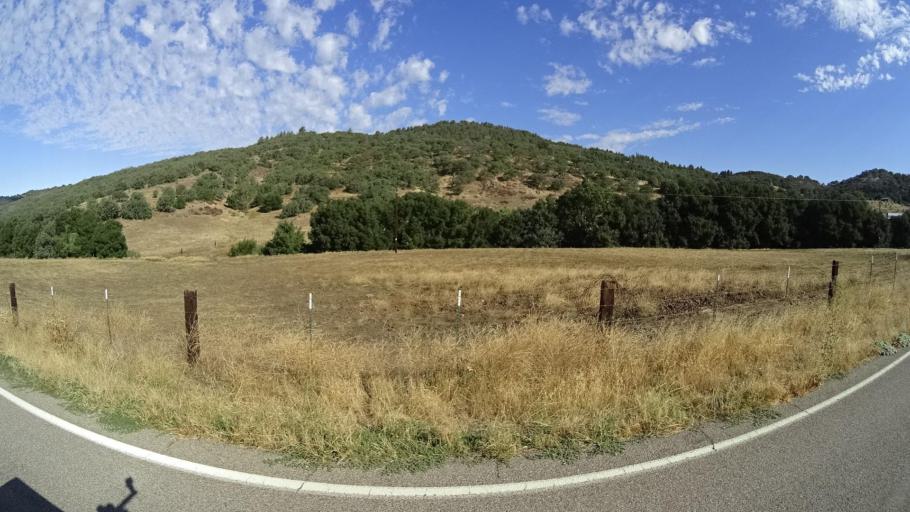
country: US
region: California
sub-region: San Diego County
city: Ramona
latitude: 33.1973
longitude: -116.7657
